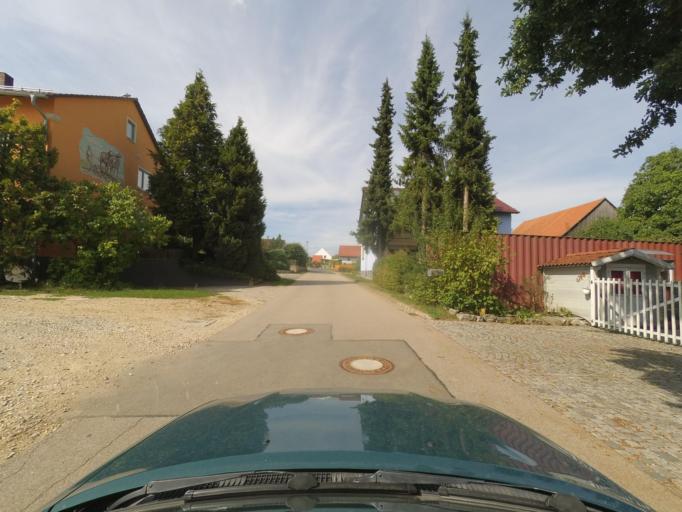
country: DE
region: Bavaria
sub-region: Upper Palatinate
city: Freystadt
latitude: 49.1747
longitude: 11.3706
